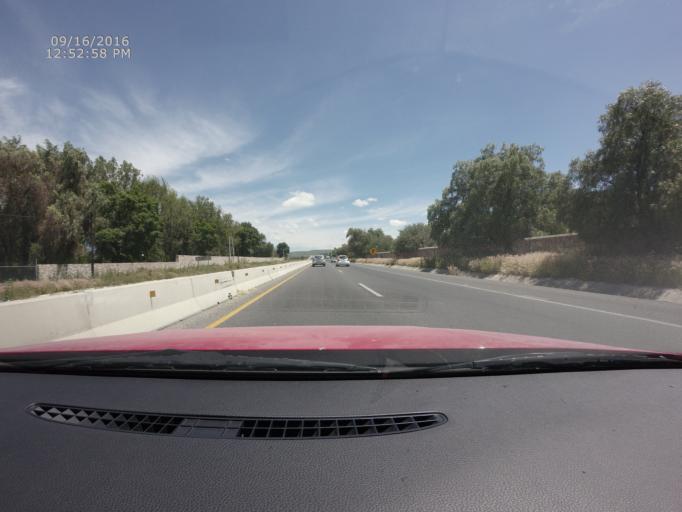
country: MX
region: Queretaro
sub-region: Colon
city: Purisima de Cubos (La Purisima)
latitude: 20.6206
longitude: -100.1355
